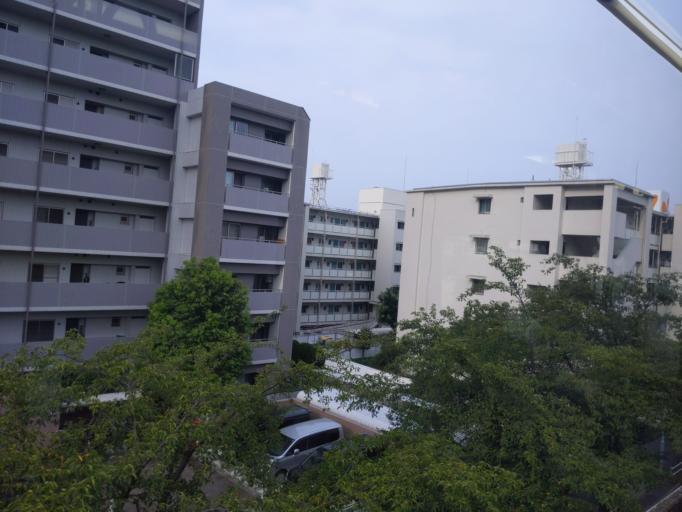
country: JP
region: Saitama
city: Shimotoda
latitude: 35.7867
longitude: 139.6765
